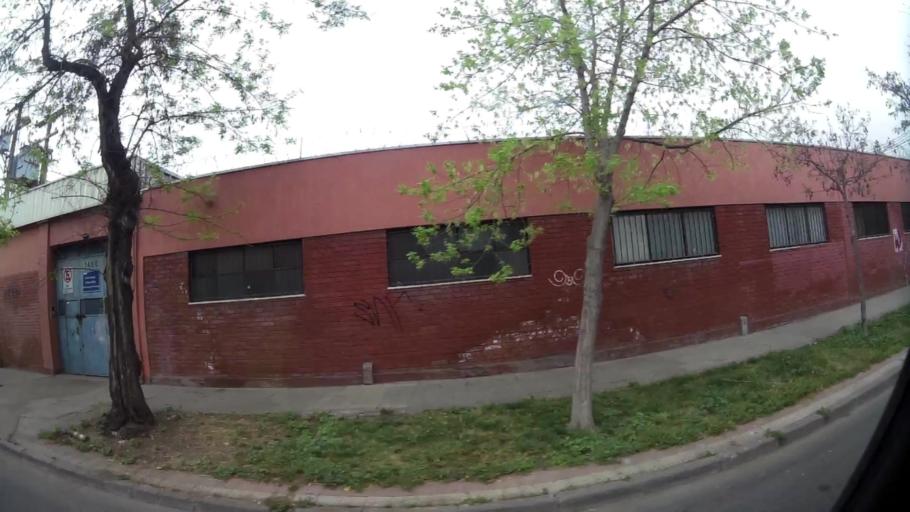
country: CL
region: Santiago Metropolitan
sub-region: Provincia de Santiago
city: Santiago
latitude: -33.4720
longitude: -70.6542
